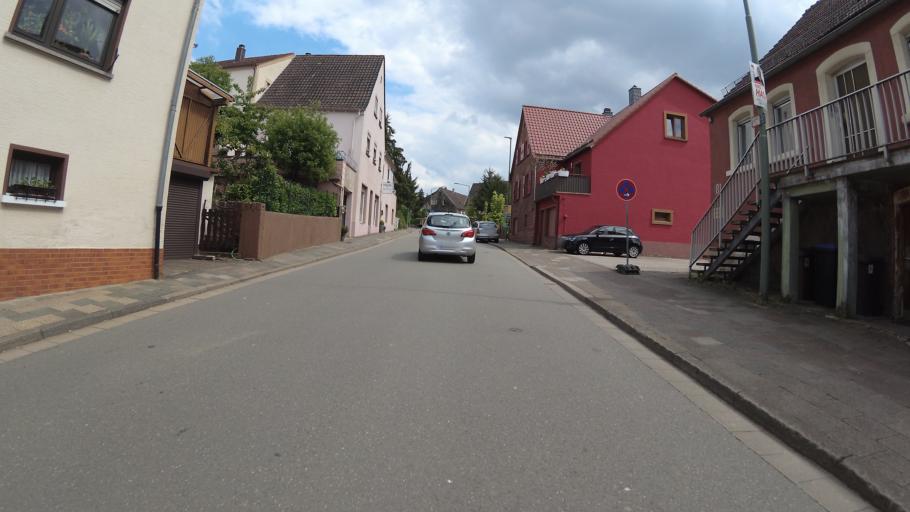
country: DE
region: Rheinland-Pfalz
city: Katzweiler
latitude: 49.4684
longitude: 7.6896
